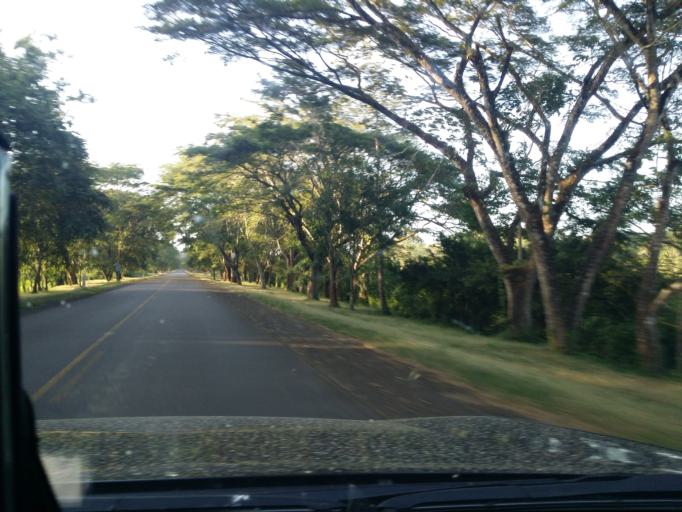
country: NI
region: Rio San Juan
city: San Miguelito
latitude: 11.4191
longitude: -84.8437
